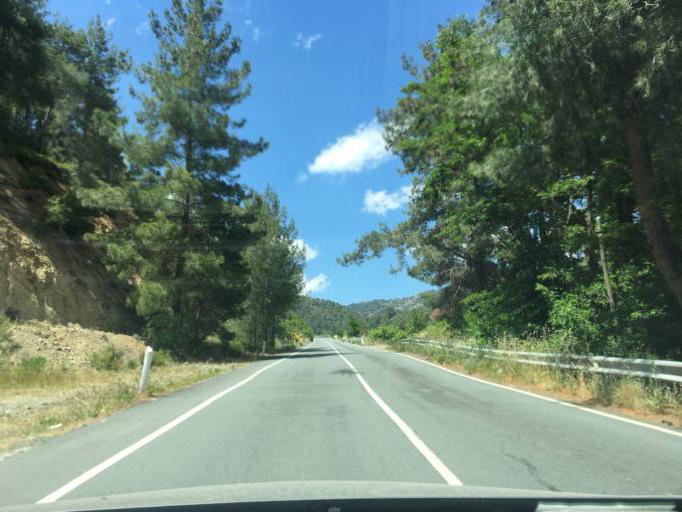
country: CY
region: Limassol
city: Pelendri
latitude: 34.9073
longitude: 32.9431
